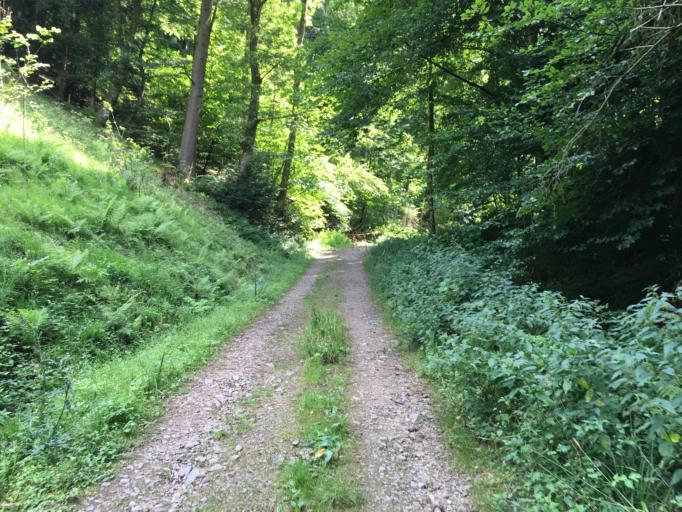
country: DE
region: Baden-Wuerttemberg
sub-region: Freiburg Region
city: Muenstertal/Schwarzwald
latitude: 47.8397
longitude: 7.8029
